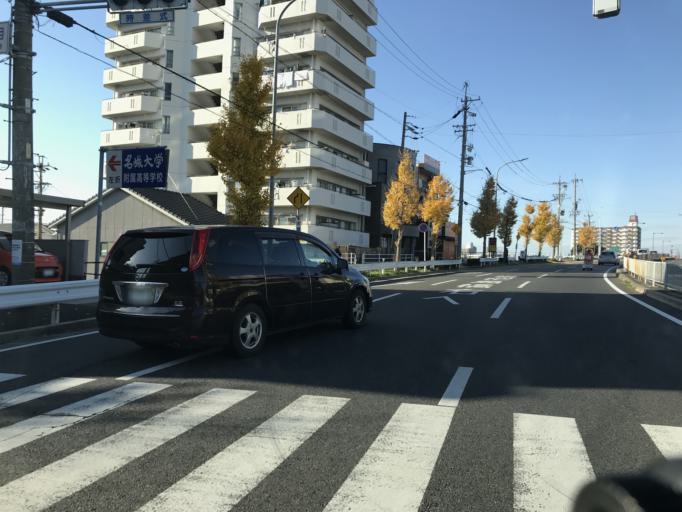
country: JP
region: Aichi
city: Nagoya-shi
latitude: 35.1902
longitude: 136.8686
